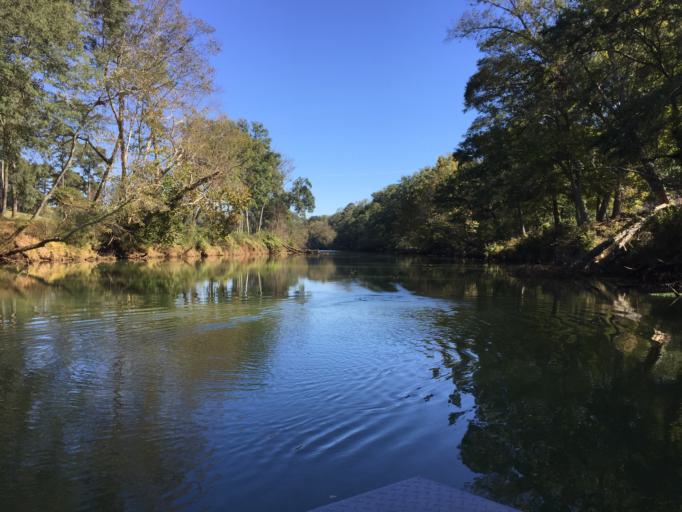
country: US
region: Georgia
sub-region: Gwinnett County
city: Berkeley Lake
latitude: 33.9938
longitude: -84.1864
